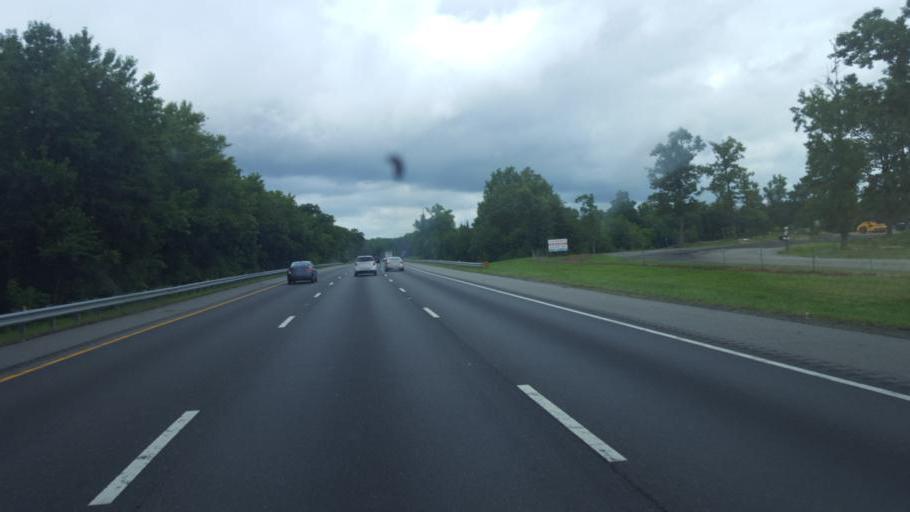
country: US
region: Virginia
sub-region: Spotsylvania County
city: Spotsylvania Courthouse
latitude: 38.1996
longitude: -77.4998
